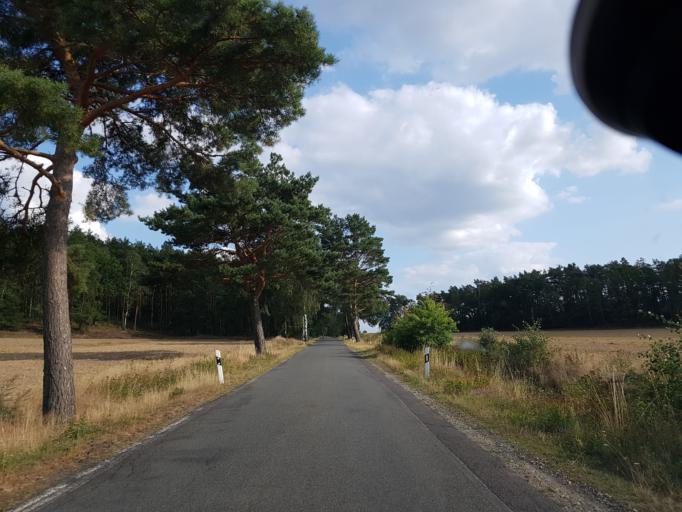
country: DE
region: Brandenburg
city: Bronkow
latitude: 51.6979
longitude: 13.8773
